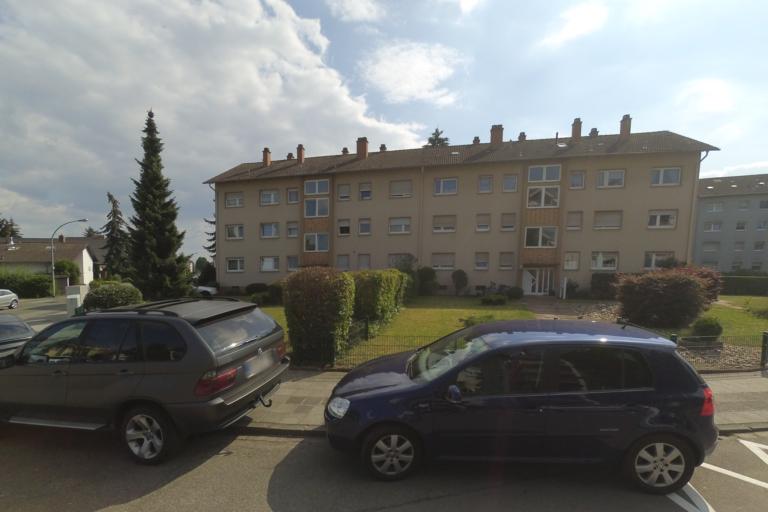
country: DE
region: Hesse
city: Viernheim
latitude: 49.5389
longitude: 8.5658
